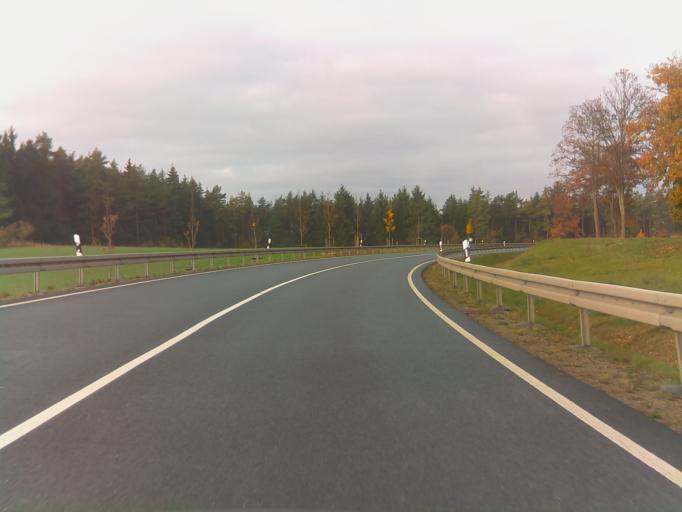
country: DE
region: Thuringia
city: Bad Blankenburg
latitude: 50.7292
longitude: 11.2254
